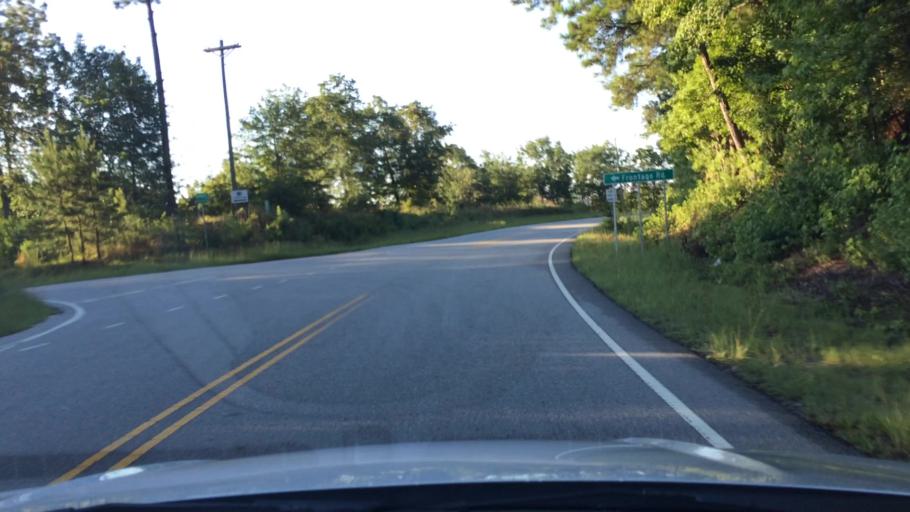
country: US
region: South Carolina
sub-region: Calhoun County
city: Oak Grove
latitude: 33.8096
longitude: -81.0090
